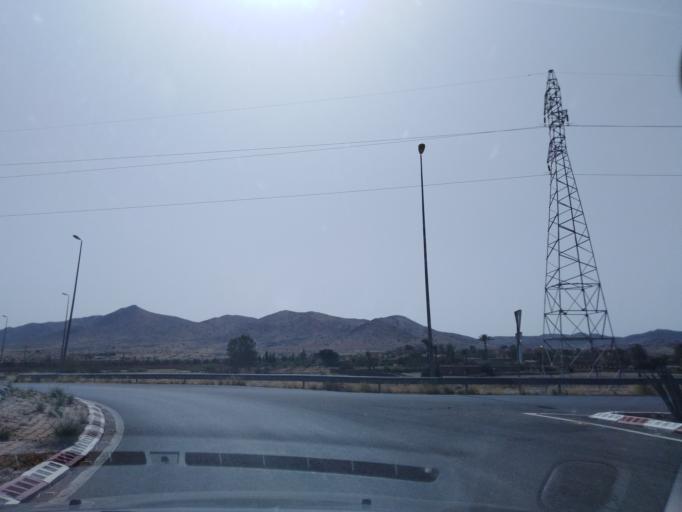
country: MA
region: Marrakech-Tensift-Al Haouz
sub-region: Marrakech
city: Marrakesh
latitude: 31.7702
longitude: -7.9811
